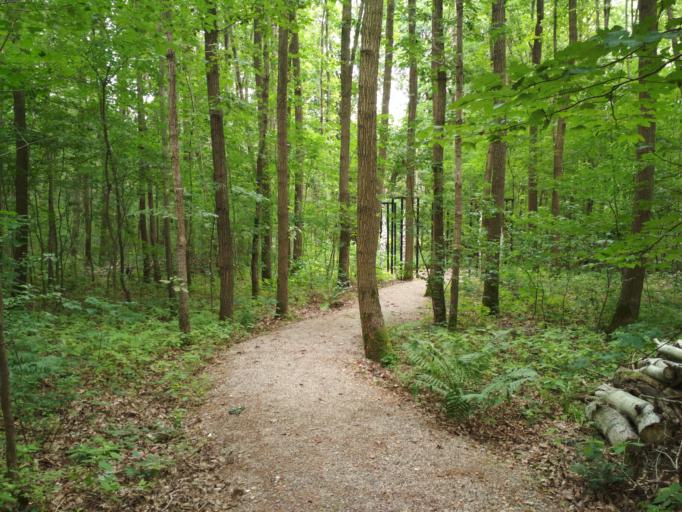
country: DE
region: Mecklenburg-Vorpommern
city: Wesenberg
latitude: 53.2887
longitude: 12.9384
